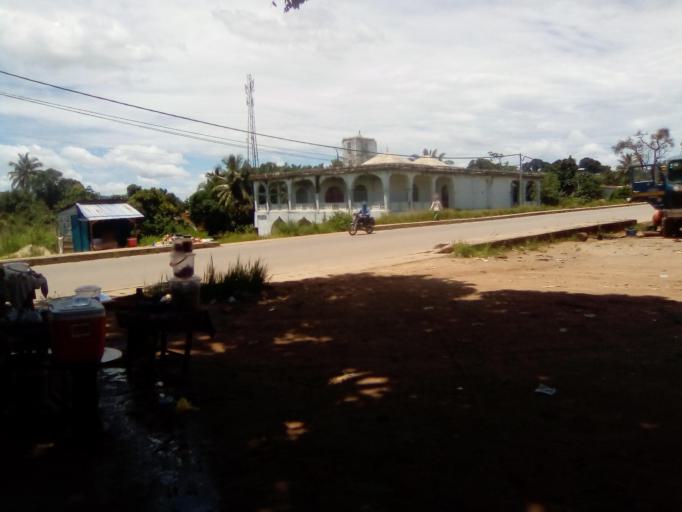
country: SL
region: Eastern Province
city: Koidu
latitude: 8.6359
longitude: -10.9830
